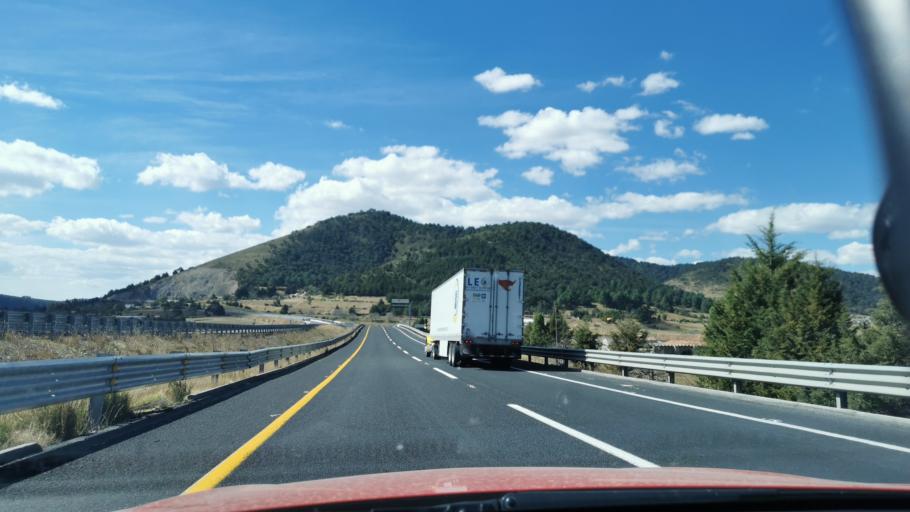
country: MX
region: Mexico
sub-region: Acambay de Ruiz Castaneda
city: La Caridad
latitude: 19.9404
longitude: -99.7845
